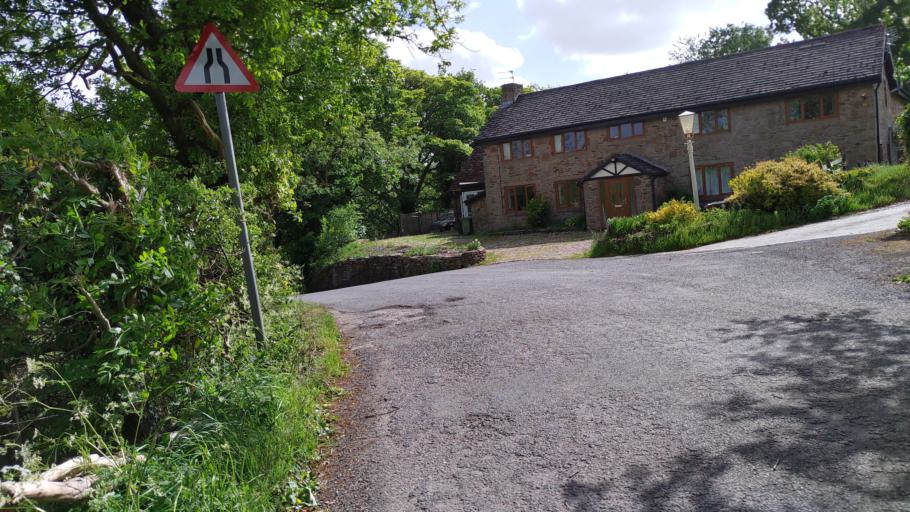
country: GB
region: England
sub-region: Lancashire
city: Chorley
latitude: 53.6429
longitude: -2.5980
